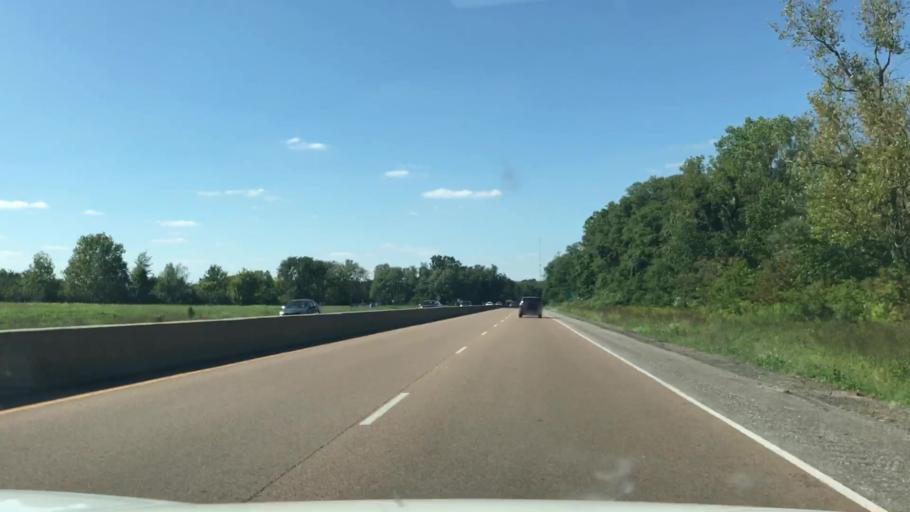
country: US
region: Illinois
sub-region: Saint Clair County
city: Alorton
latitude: 38.5544
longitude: -90.0760
